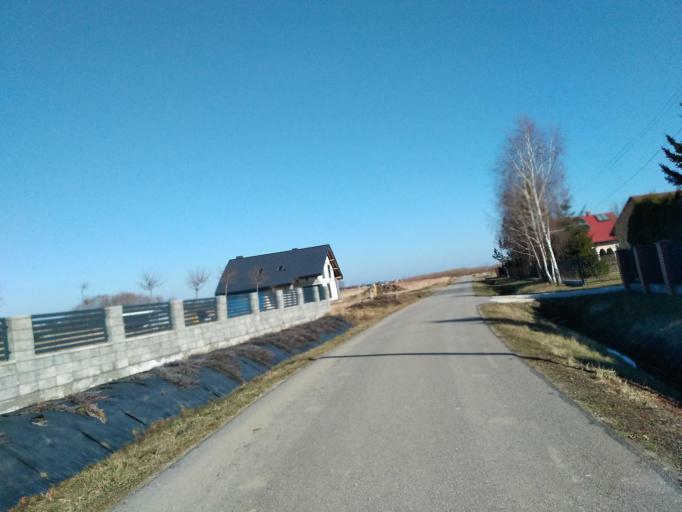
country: PL
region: Subcarpathian Voivodeship
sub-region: Powiat rzeszowski
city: Lutoryz
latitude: 49.9557
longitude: 21.9222
